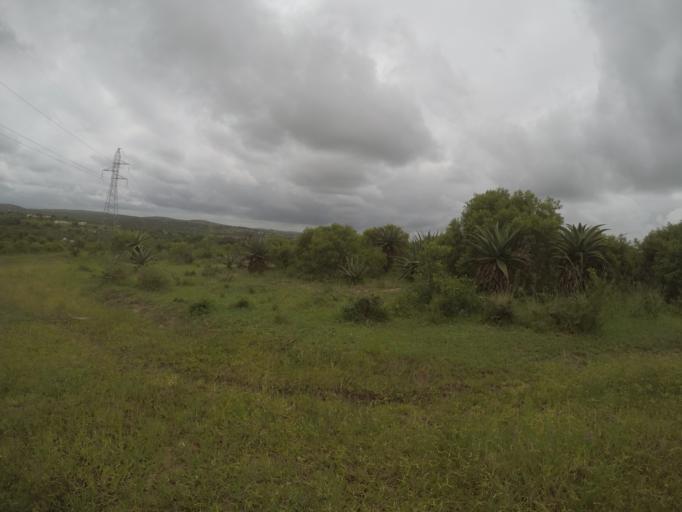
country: ZA
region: KwaZulu-Natal
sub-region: uThungulu District Municipality
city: Empangeni
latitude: -28.5975
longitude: 31.8448
